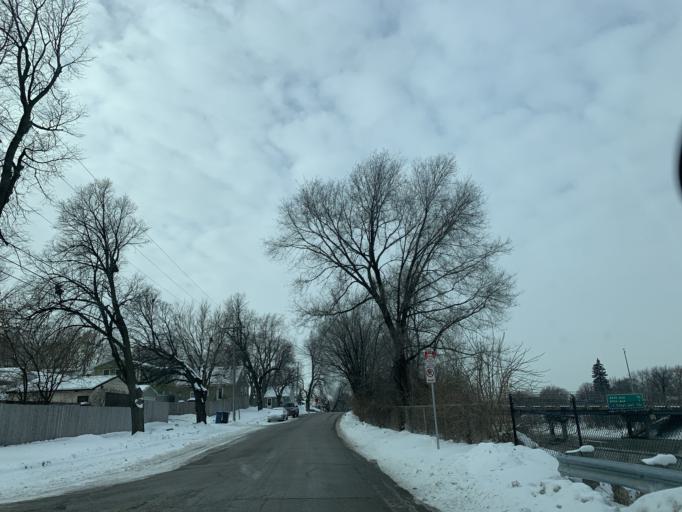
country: US
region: Minnesota
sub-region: Dakota County
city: Mendota Heights
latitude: 44.8982
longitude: -93.2102
